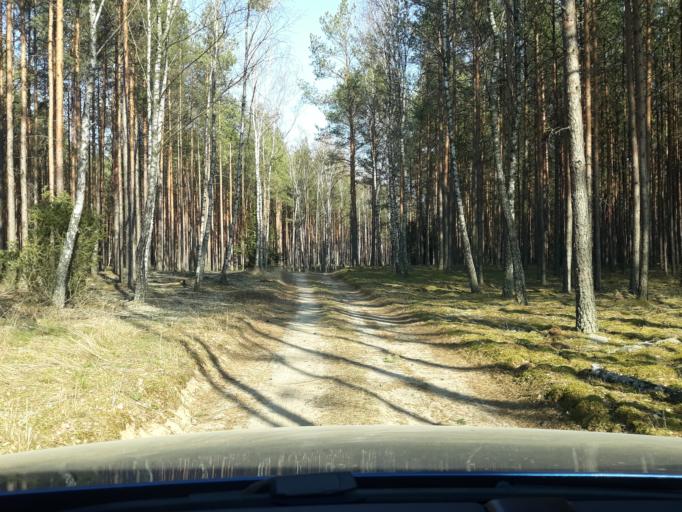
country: PL
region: Pomeranian Voivodeship
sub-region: Powiat bytowski
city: Lipnica
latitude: 53.9188
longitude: 17.4605
